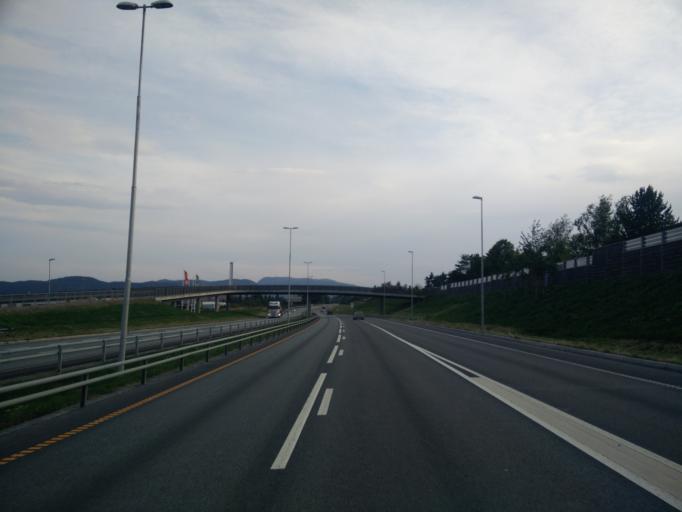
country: NO
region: Sor-Trondelag
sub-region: Trondheim
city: Trondheim
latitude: 63.3581
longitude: 10.3713
